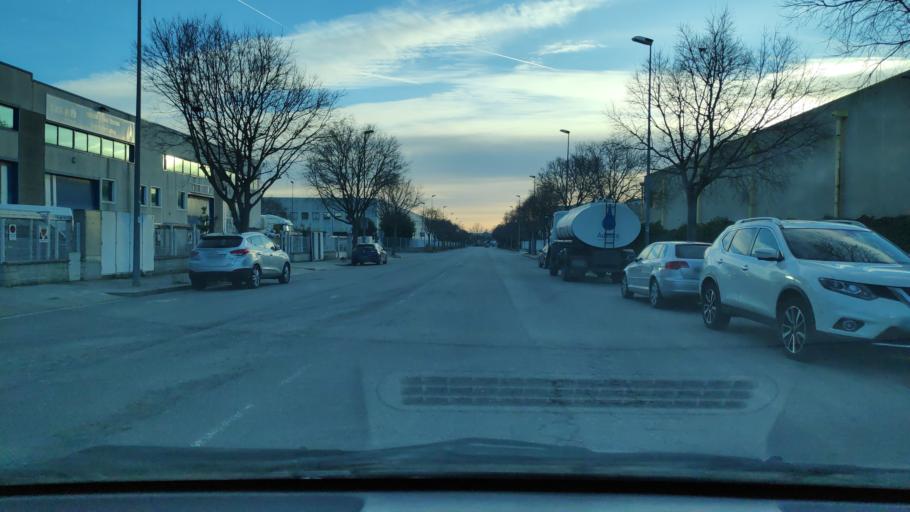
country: ES
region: Catalonia
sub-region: Provincia de Barcelona
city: Montmelo
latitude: 41.5692
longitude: 2.2662
